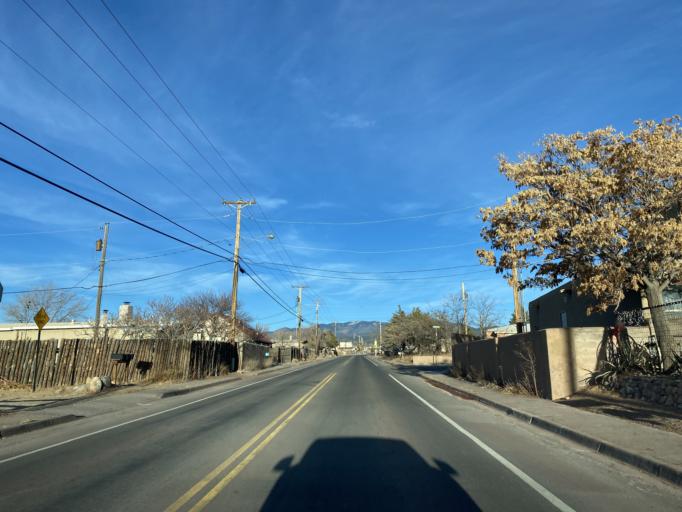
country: US
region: New Mexico
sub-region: Santa Fe County
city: Santa Fe
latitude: 35.6753
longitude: -105.9738
